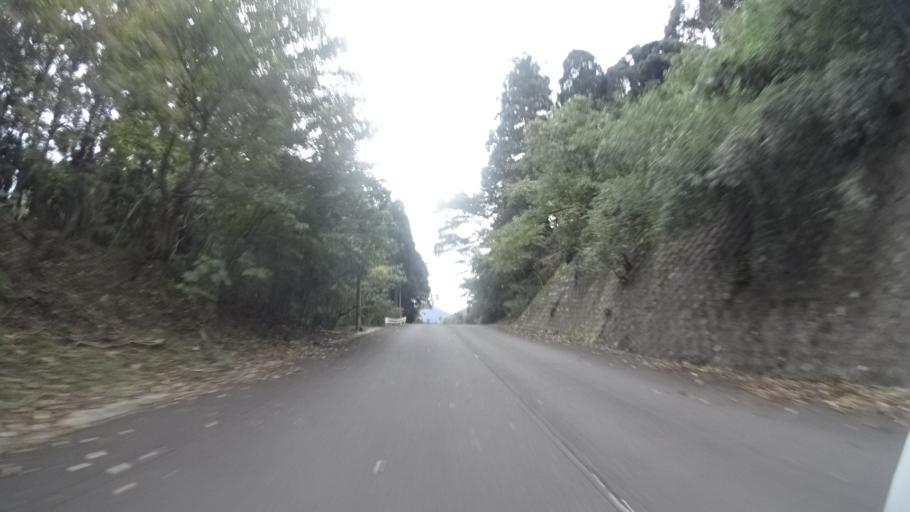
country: JP
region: Kyoto
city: Maizuru
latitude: 35.5679
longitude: 135.4622
